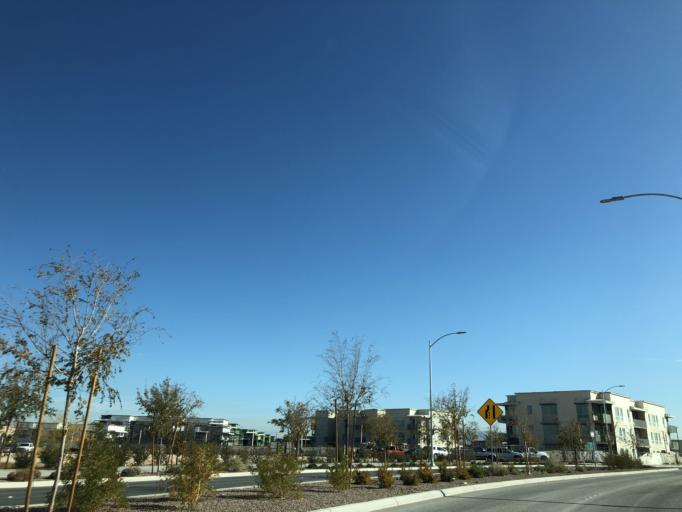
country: US
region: Nevada
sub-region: Clark County
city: Whitney
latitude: 36.0773
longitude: -115.0366
